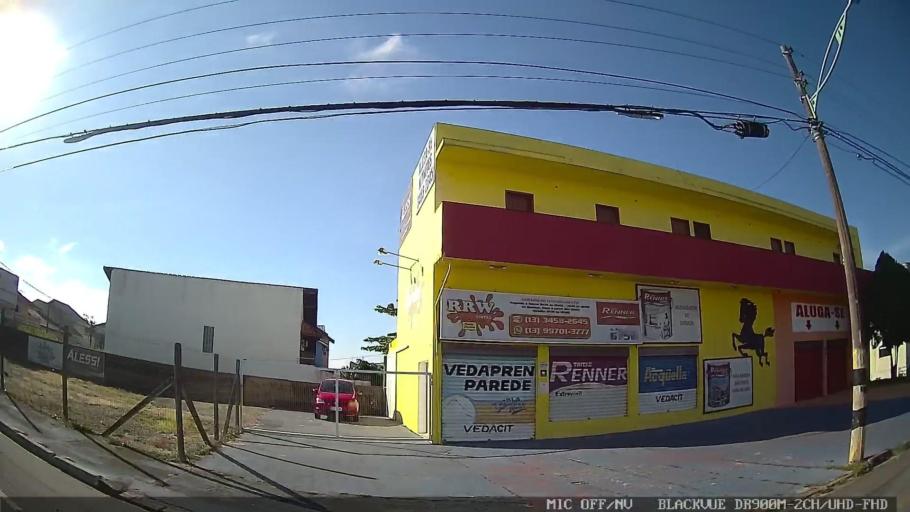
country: BR
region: Sao Paulo
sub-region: Peruibe
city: Peruibe
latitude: -24.2852
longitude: -46.9552
